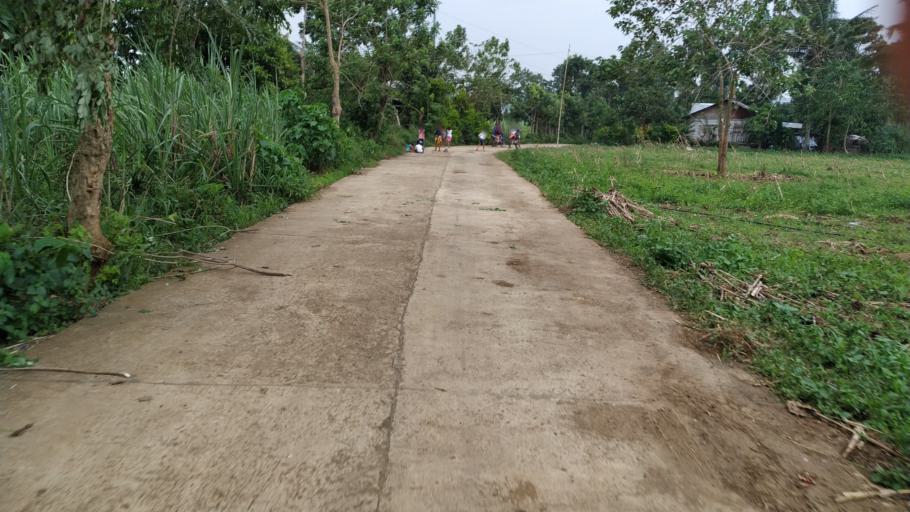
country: PH
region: Western Visayas
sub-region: Province of Negros Occidental
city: Quezon
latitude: 10.4250
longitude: 123.2340
